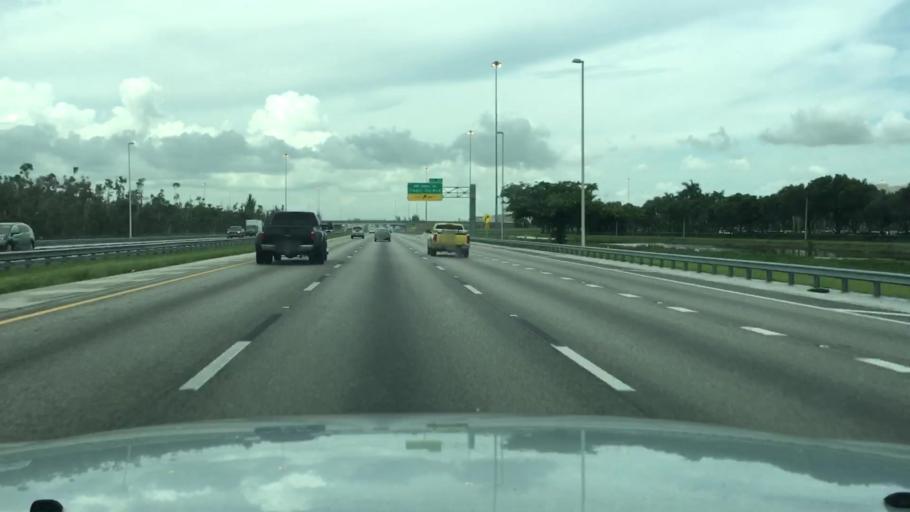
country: US
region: Florida
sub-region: Miami-Dade County
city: Doral
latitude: 25.8586
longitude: -80.3939
